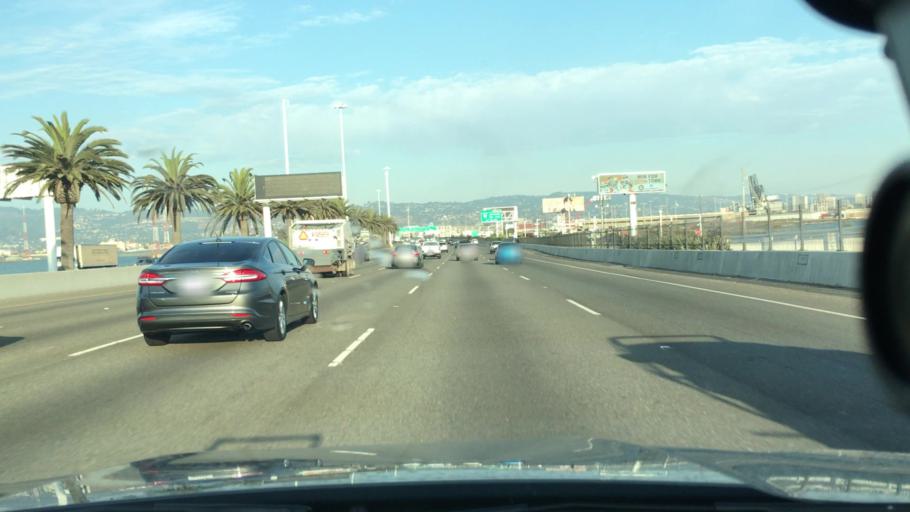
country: US
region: California
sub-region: Alameda County
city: Emeryville
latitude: 37.8202
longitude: -122.3261
